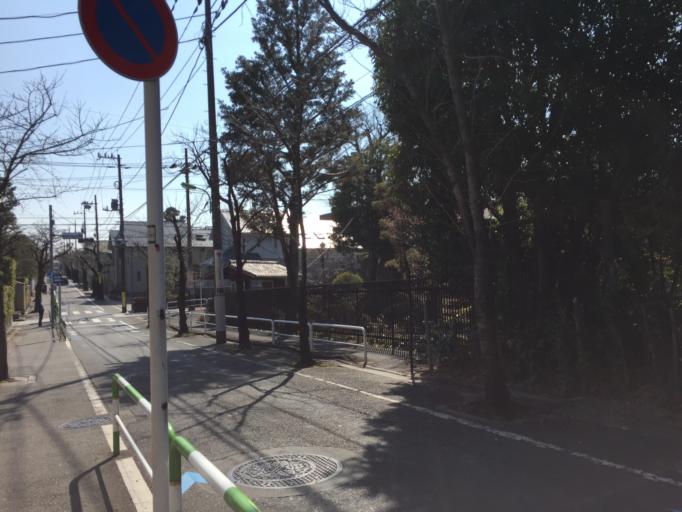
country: JP
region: Tokyo
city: Tokyo
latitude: 35.6252
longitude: 139.6463
